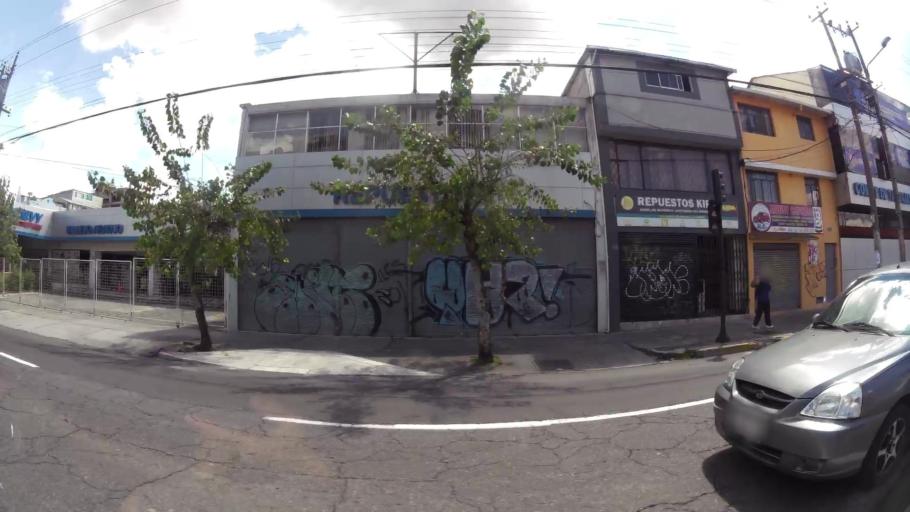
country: EC
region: Pichincha
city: Quito
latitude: -0.1924
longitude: -78.4939
